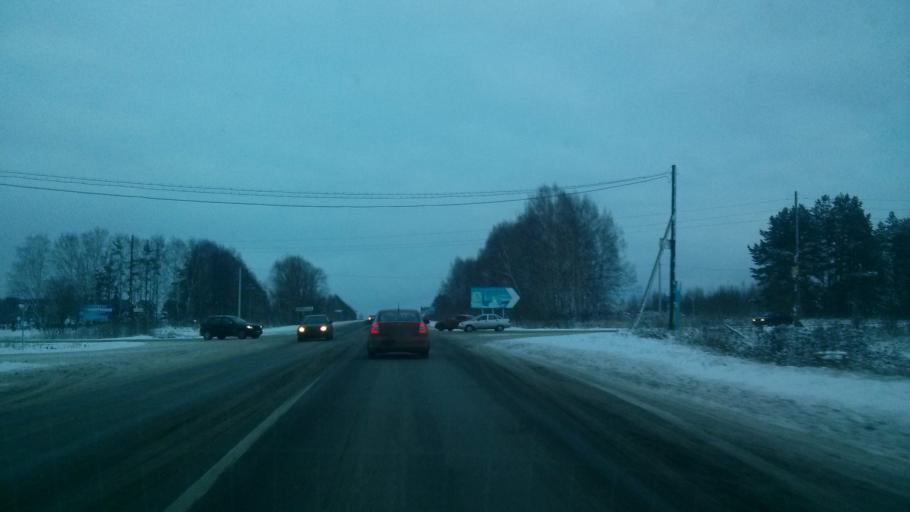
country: RU
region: Nizjnij Novgorod
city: Bogorodsk
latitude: 56.0869
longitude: 43.5275
